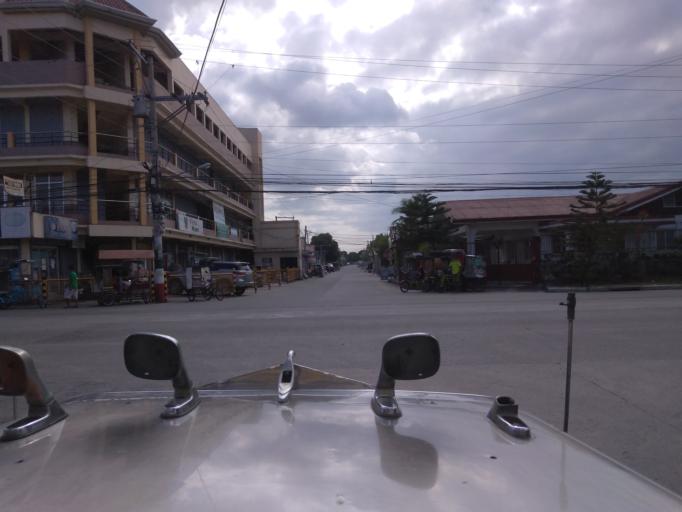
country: PH
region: Central Luzon
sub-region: Province of Pampanga
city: Pandacaqui
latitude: 15.1794
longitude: 120.6441
